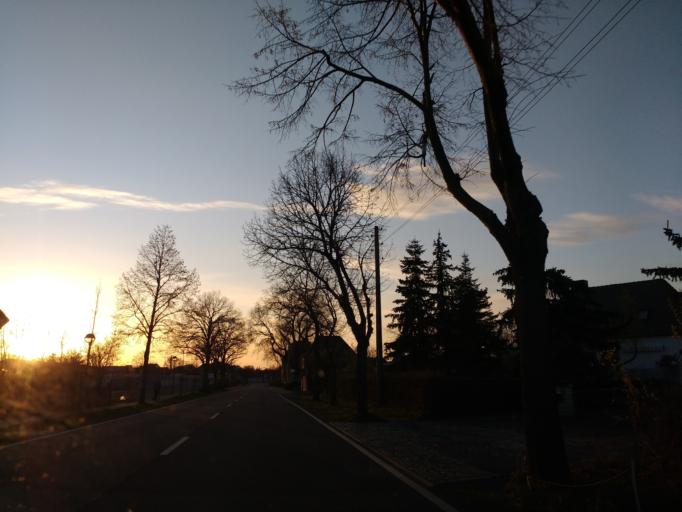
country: DE
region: Saxony-Anhalt
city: Zorbig
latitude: 51.6270
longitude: 12.1283
